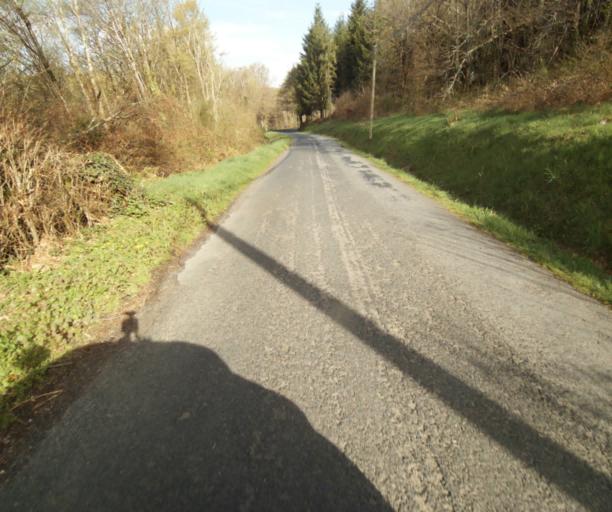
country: FR
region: Limousin
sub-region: Departement de la Correze
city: Naves
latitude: 45.3324
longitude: 1.8247
